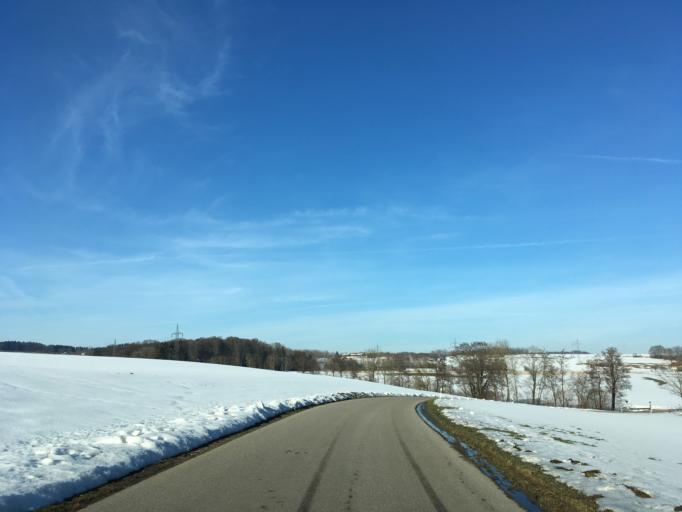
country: DE
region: Bavaria
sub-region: Upper Bavaria
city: Steinhoring
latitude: 48.1001
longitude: 12.0201
